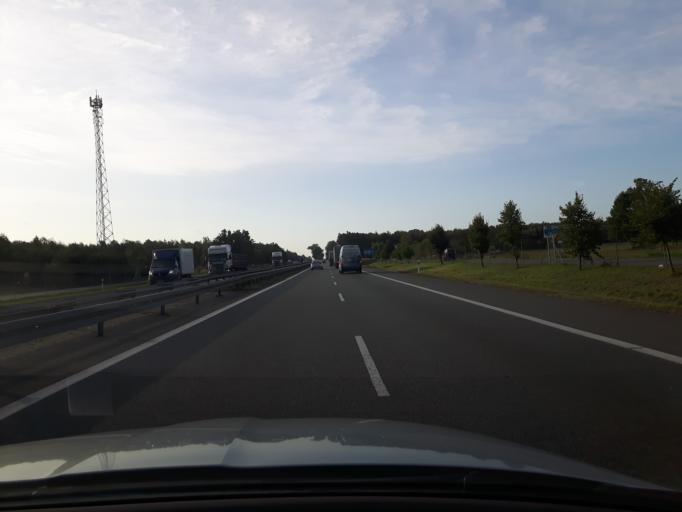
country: PL
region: Masovian Voivodeship
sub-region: Powiat bialobrzeski
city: Sucha
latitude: 51.6033
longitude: 20.9864
